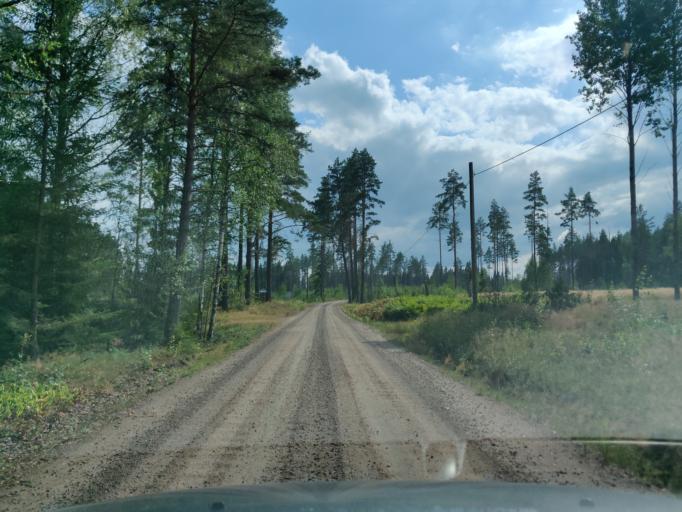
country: SE
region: Vaermland
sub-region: Hagfors Kommun
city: Hagfors
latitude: 59.9905
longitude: 13.5654
